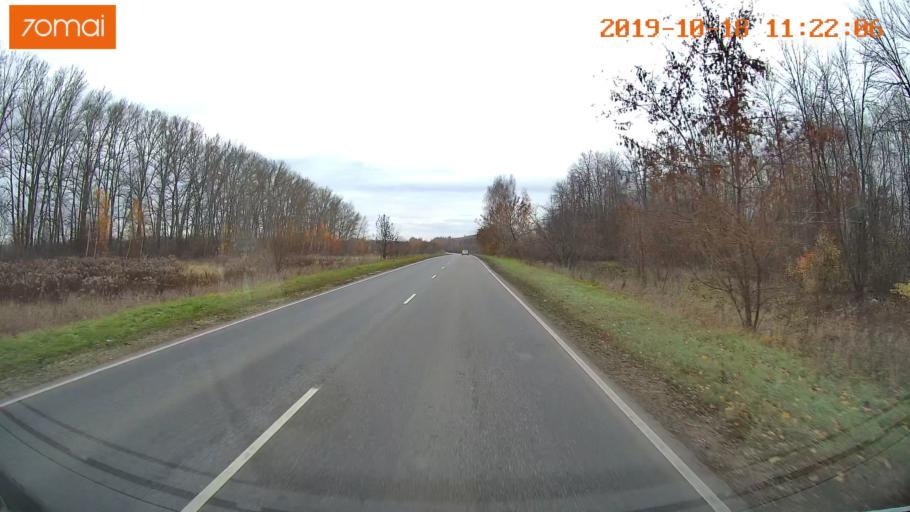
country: RU
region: Tula
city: Kimovsk
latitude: 54.0828
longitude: 38.5754
